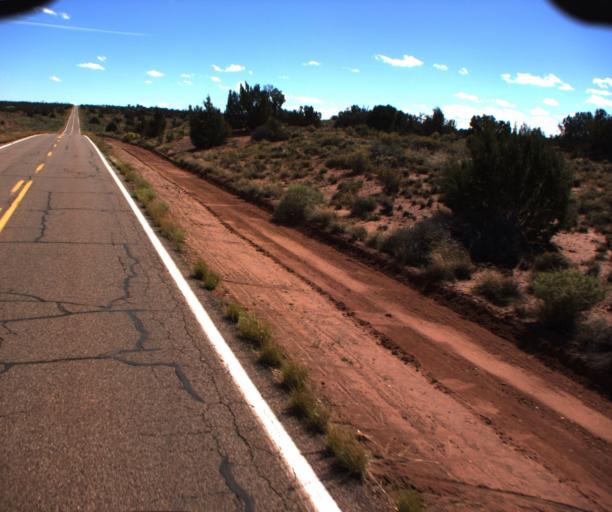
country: US
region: Arizona
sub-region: Apache County
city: Saint Johns
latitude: 34.6010
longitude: -109.6524
